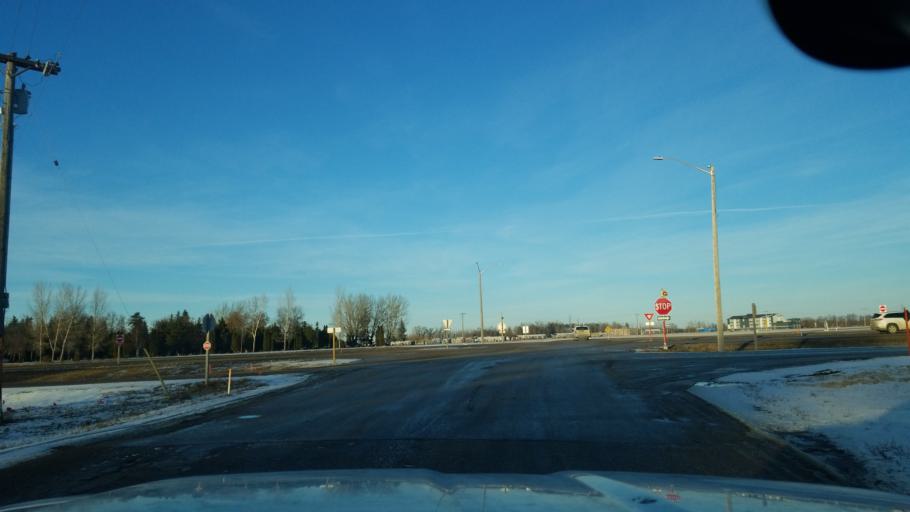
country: CA
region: Manitoba
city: Portage la Prairie
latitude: 49.9542
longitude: -98.3287
